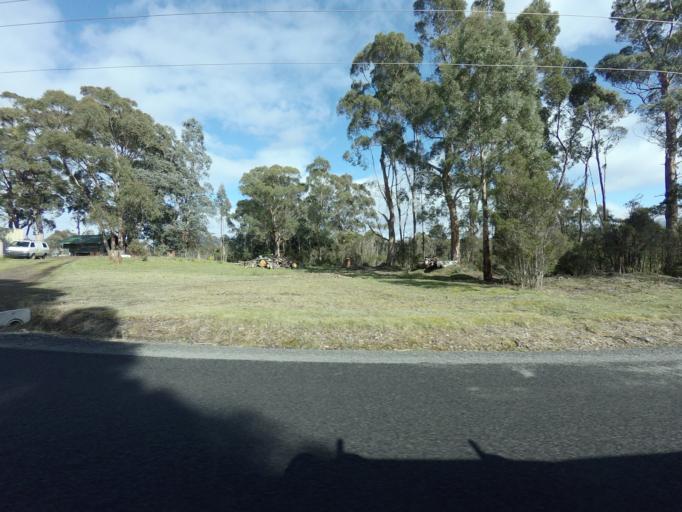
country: AU
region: Tasmania
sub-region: Huon Valley
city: Geeveston
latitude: -43.4320
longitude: 146.9035
